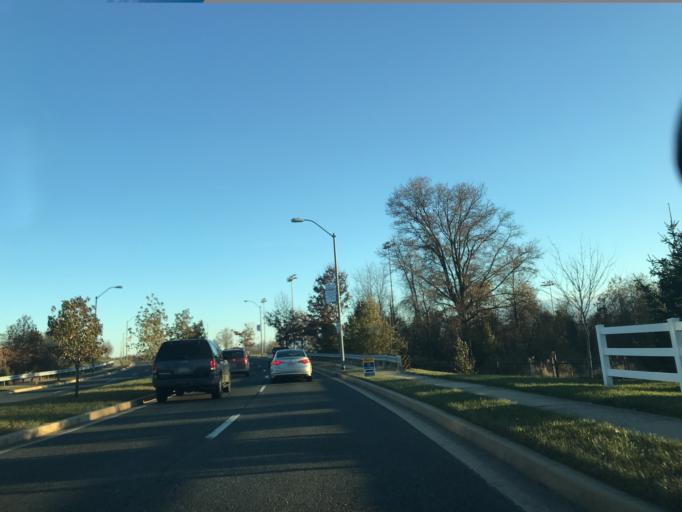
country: US
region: Maryland
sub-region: Baltimore County
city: Perry Hall
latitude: 39.4155
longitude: -76.4530
